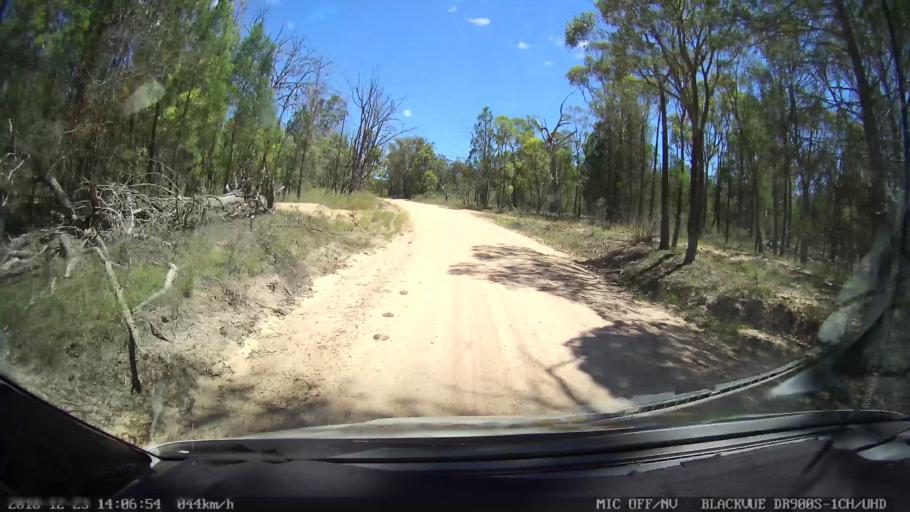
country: AU
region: New South Wales
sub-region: Tamworth Municipality
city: Manilla
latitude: -30.6326
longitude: 151.0738
